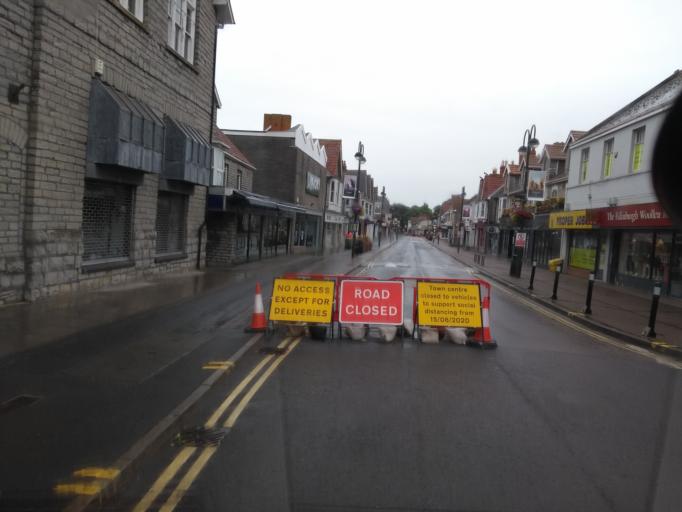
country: GB
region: England
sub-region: Somerset
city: Street
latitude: 51.1257
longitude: -2.7422
